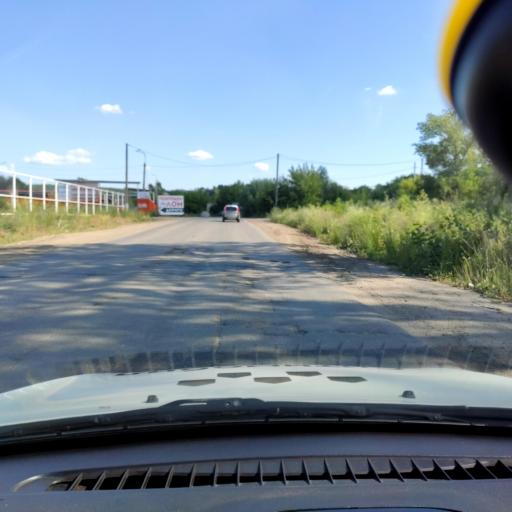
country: RU
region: Samara
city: Zhigulevsk
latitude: 53.4097
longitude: 49.4884
